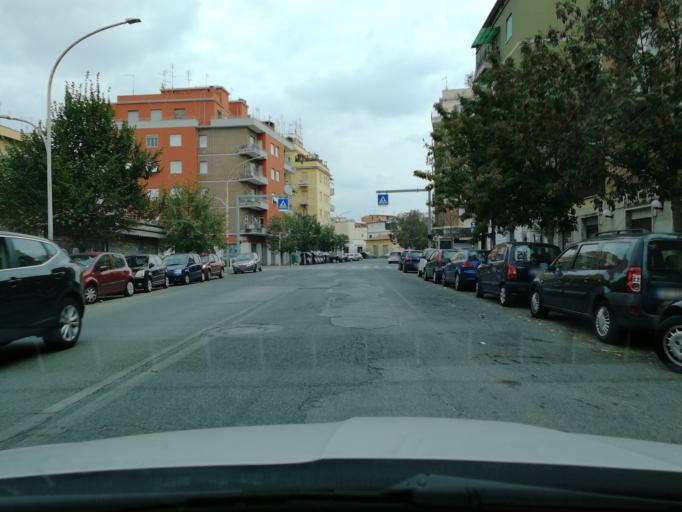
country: IT
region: Latium
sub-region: Citta metropolitana di Roma Capitale
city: Rome
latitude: 41.8613
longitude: 12.5491
